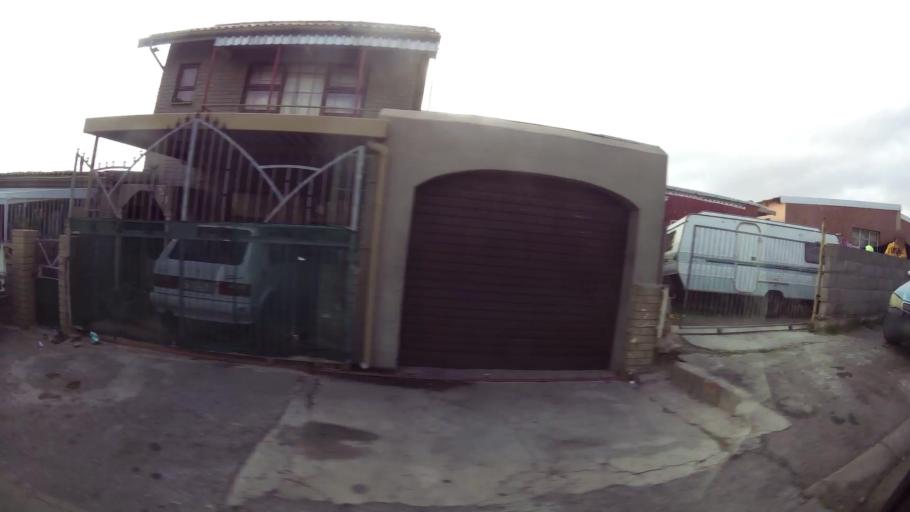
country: ZA
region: Eastern Cape
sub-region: Nelson Mandela Bay Metropolitan Municipality
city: Port Elizabeth
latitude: -33.9186
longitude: 25.5445
